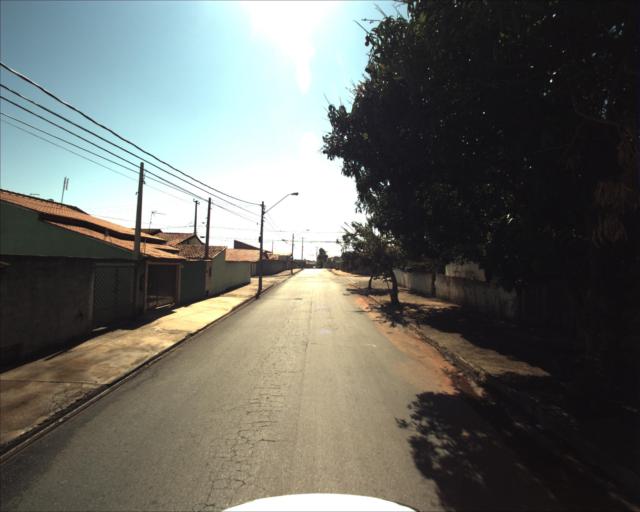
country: BR
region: Sao Paulo
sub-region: Sorocaba
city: Sorocaba
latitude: -23.4679
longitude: -47.4870
